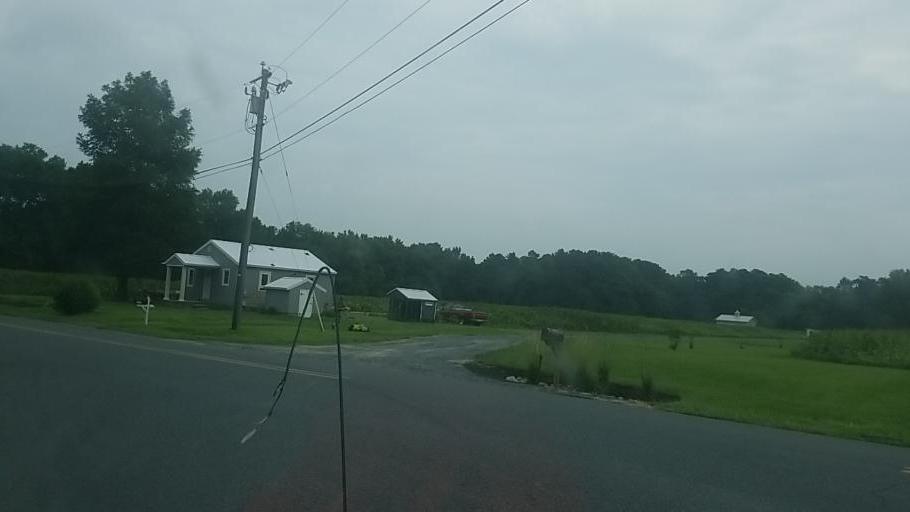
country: US
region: Delaware
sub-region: Sussex County
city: Selbyville
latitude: 38.4418
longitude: -75.2225
